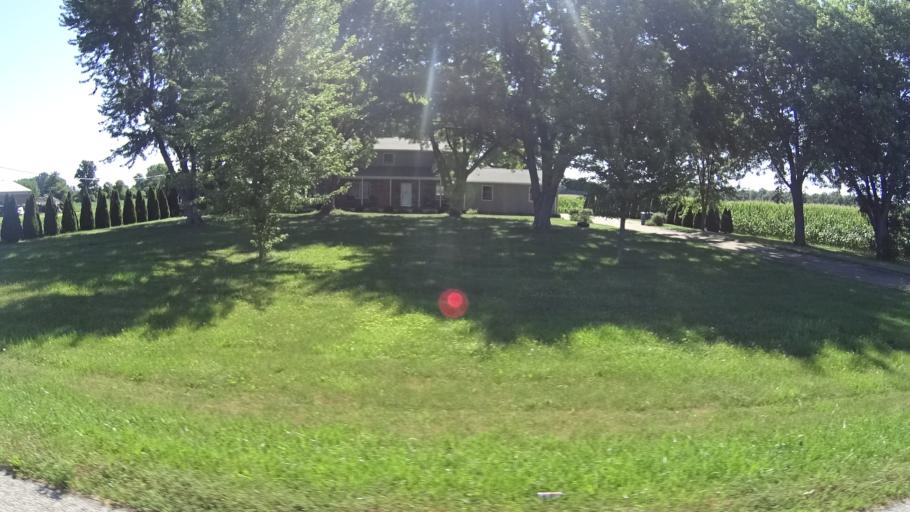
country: US
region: Ohio
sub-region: Erie County
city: Sandusky
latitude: 41.3827
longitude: -82.7229
